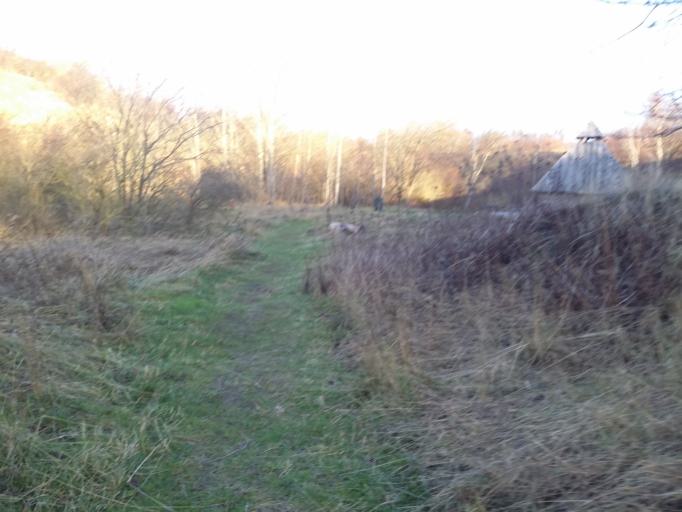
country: DK
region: Capital Region
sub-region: Frederikssund Kommune
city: Frederikssund
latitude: 55.8334
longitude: 12.0926
